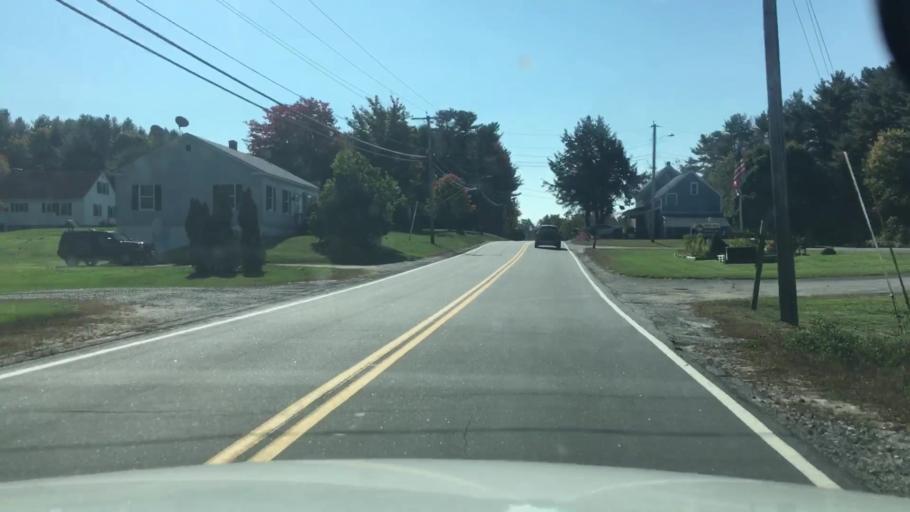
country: US
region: Maine
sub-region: Androscoggin County
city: Lisbon Falls
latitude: 44.0144
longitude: -70.0488
